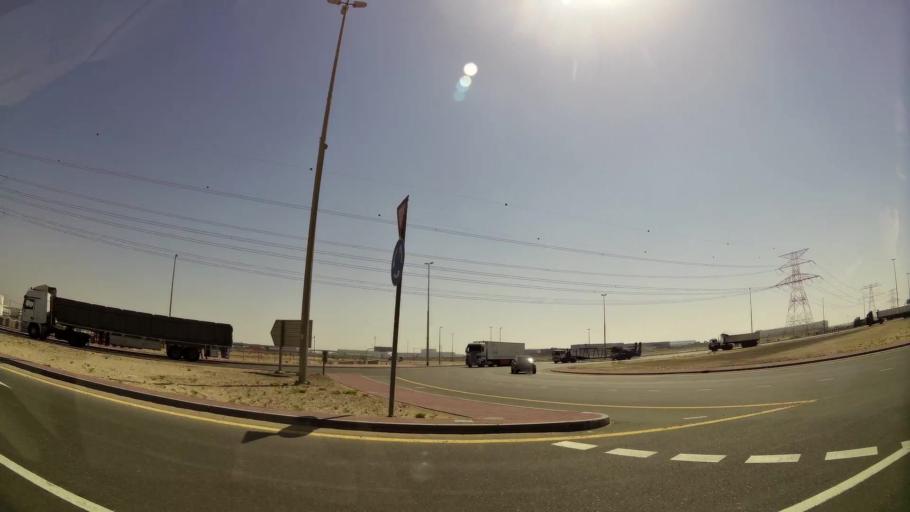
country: AE
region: Dubai
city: Dubai
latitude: 24.9270
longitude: 55.0913
